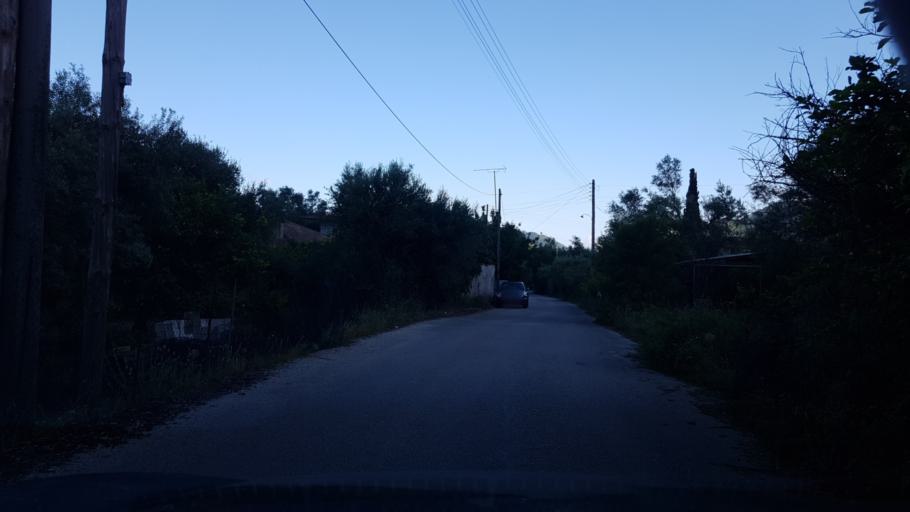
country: GR
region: Ionian Islands
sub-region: Lefkada
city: Nidri
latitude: 38.7175
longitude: 20.6953
